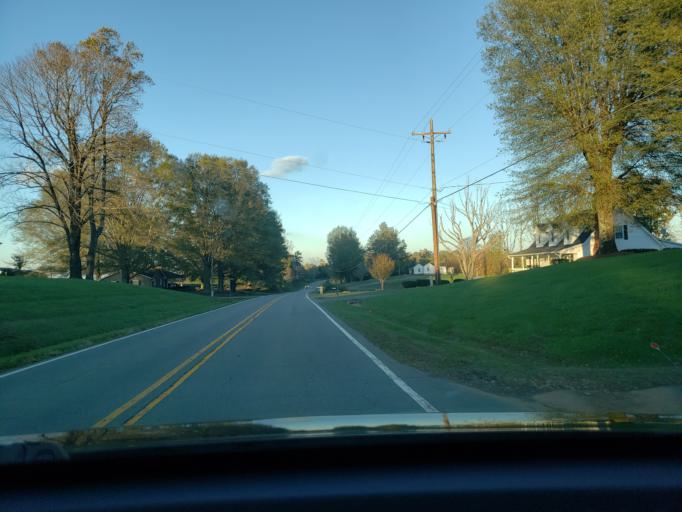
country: US
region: North Carolina
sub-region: Stokes County
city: Danbury
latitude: 36.3597
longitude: -80.2102
